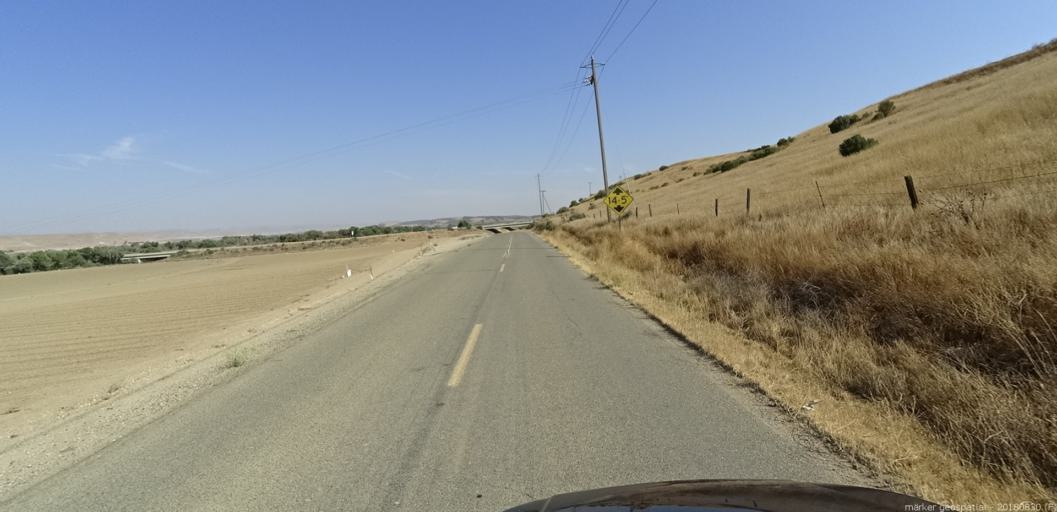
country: US
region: California
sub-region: Monterey County
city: King City
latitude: 36.1064
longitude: -121.0280
